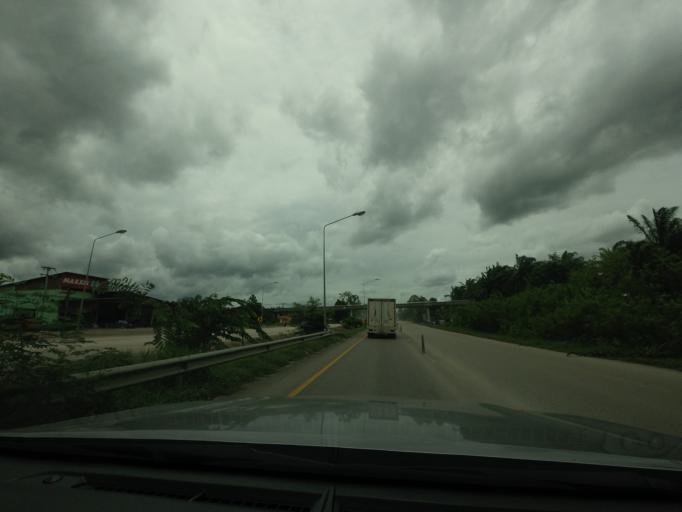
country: TH
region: Chumphon
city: Lamae
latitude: 9.7506
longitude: 99.0903
